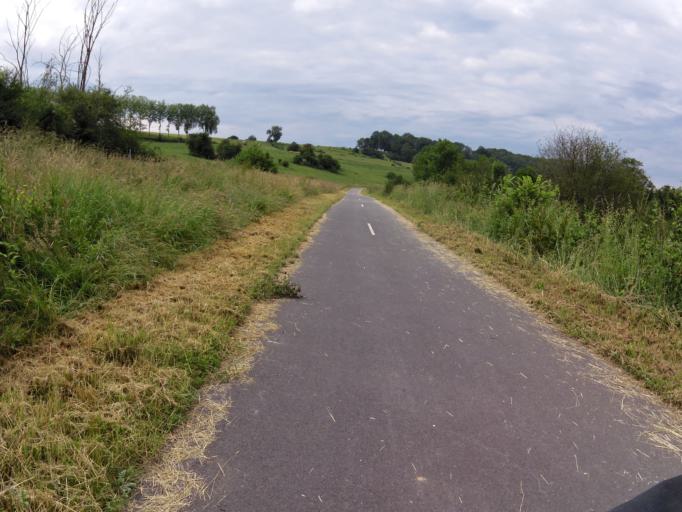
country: FR
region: Champagne-Ardenne
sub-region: Departement des Ardennes
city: Donchery
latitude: 49.6946
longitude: 4.8983
